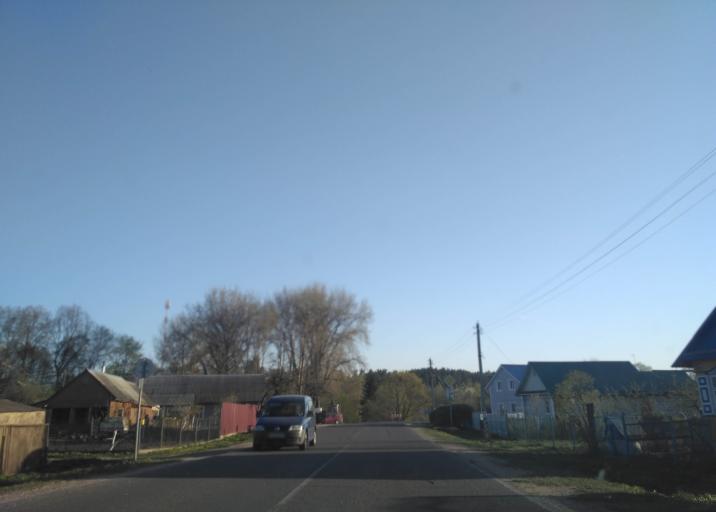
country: BY
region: Minsk
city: Pyatryshki
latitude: 54.1114
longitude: 27.1909
